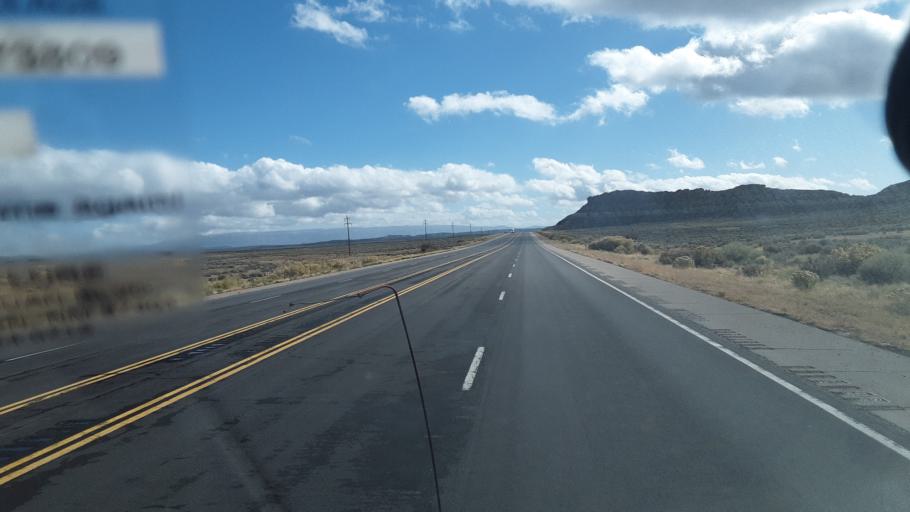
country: US
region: New Mexico
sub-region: Rio Arriba County
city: Santa Teresa
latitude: 36.1431
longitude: -107.2535
